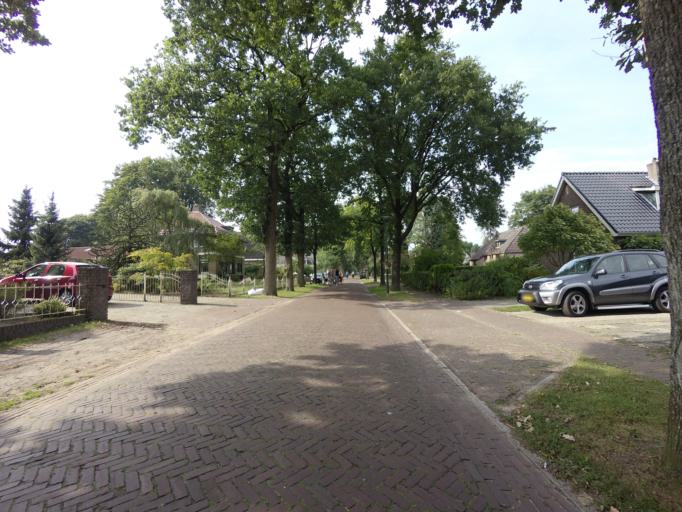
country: NL
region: Friesland
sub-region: Gemeente Weststellingwerf
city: Noordwolde
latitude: 52.9209
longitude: 6.2565
